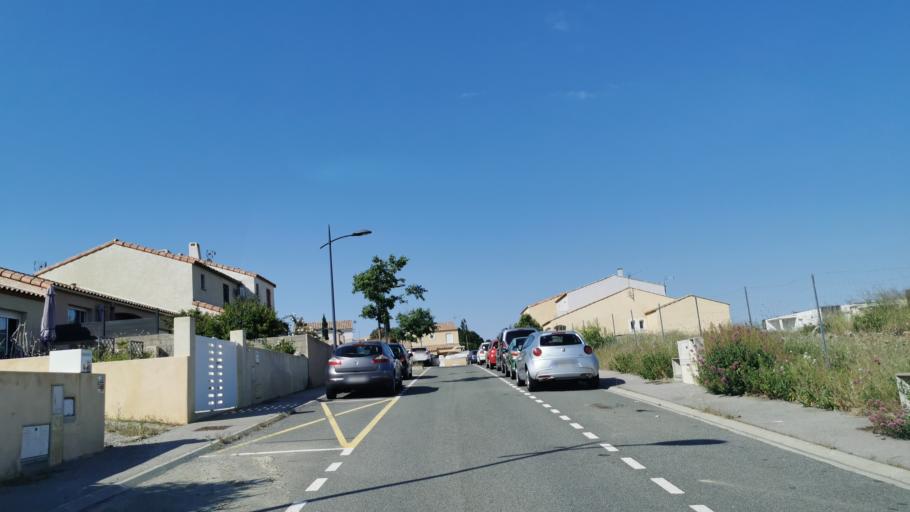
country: FR
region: Languedoc-Roussillon
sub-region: Departement de l'Aude
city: Peyriac-de-Mer
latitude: 43.1362
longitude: 2.9650
